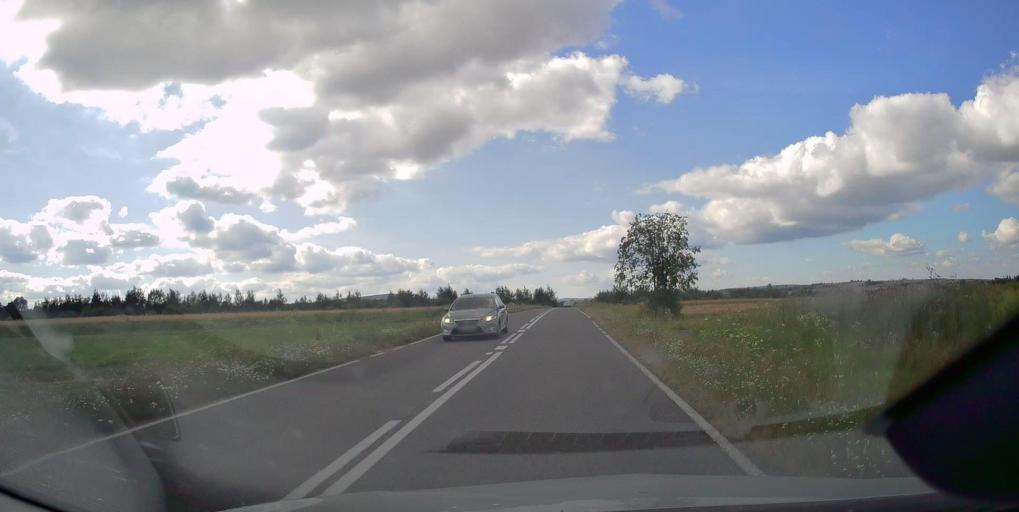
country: PL
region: Swietokrzyskie
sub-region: Powiat kielecki
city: Bodzentyn
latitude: 50.9036
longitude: 21.0129
